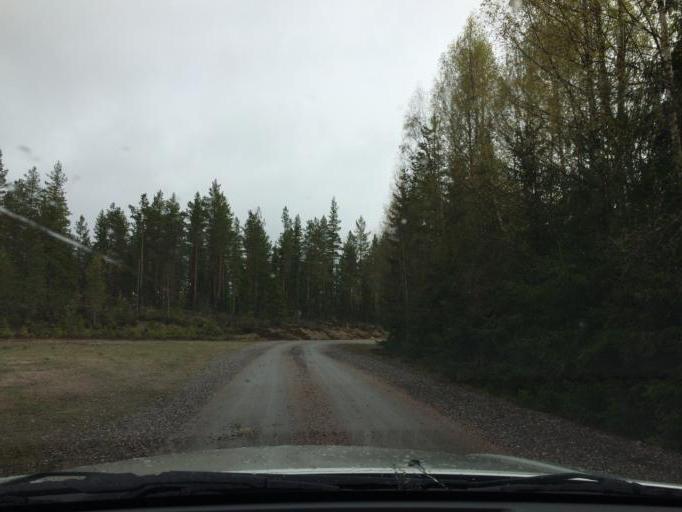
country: SE
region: OErebro
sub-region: Hallefors Kommun
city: Haellefors
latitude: 60.0160
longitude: 14.5870
